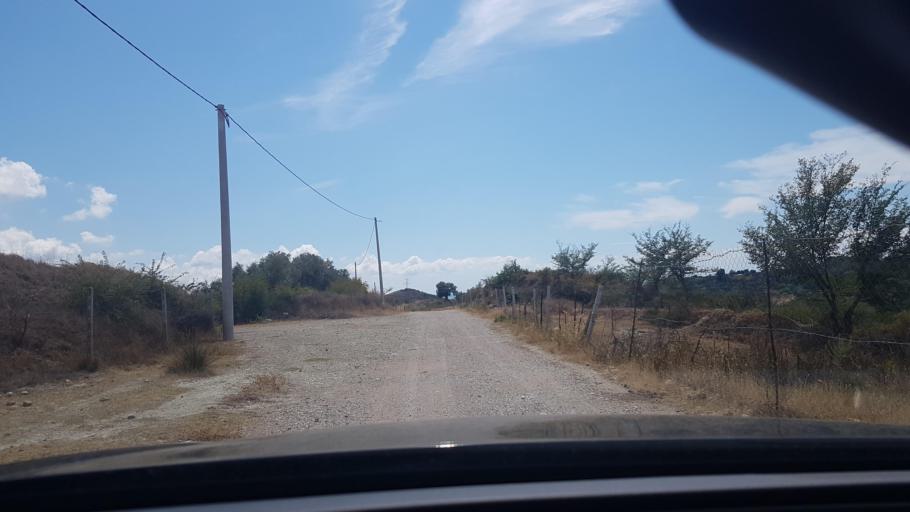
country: AL
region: Tirane
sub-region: Rrethi i Kavajes
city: Golem
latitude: 41.2859
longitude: 19.5478
